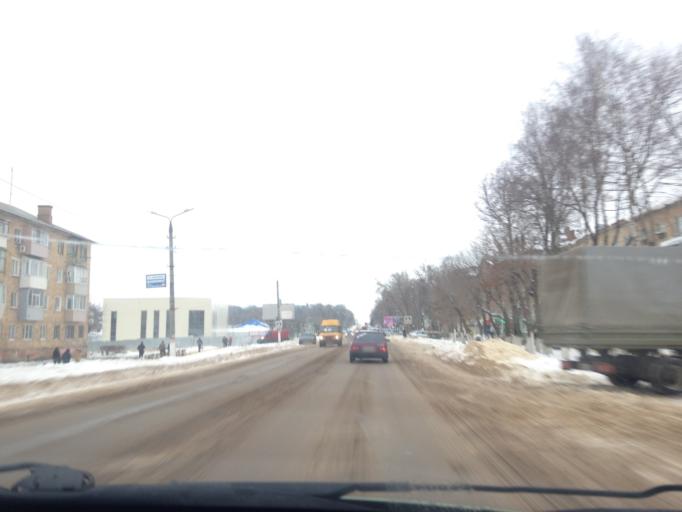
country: RU
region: Tula
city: Shchekino
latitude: 54.0083
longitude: 37.5133
